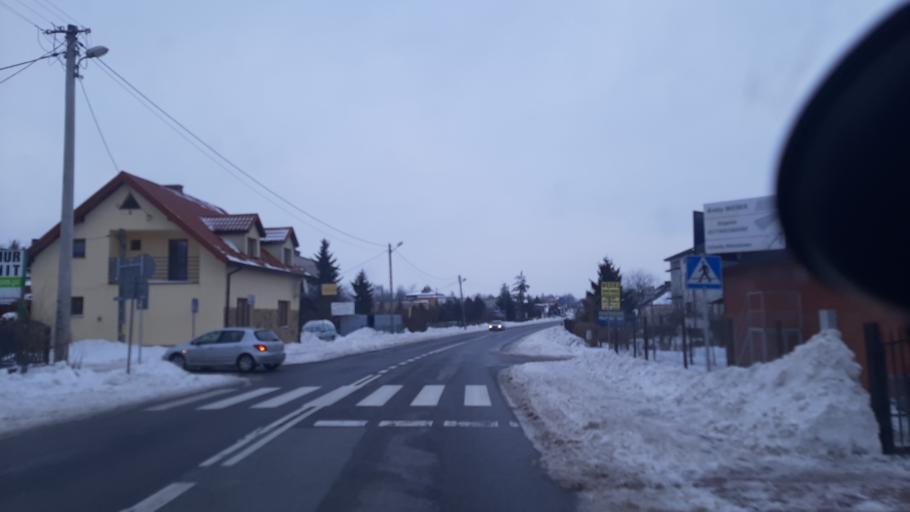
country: PL
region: Lublin Voivodeship
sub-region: Powiat pulawski
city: Markuszow
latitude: 51.3740
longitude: 22.2643
